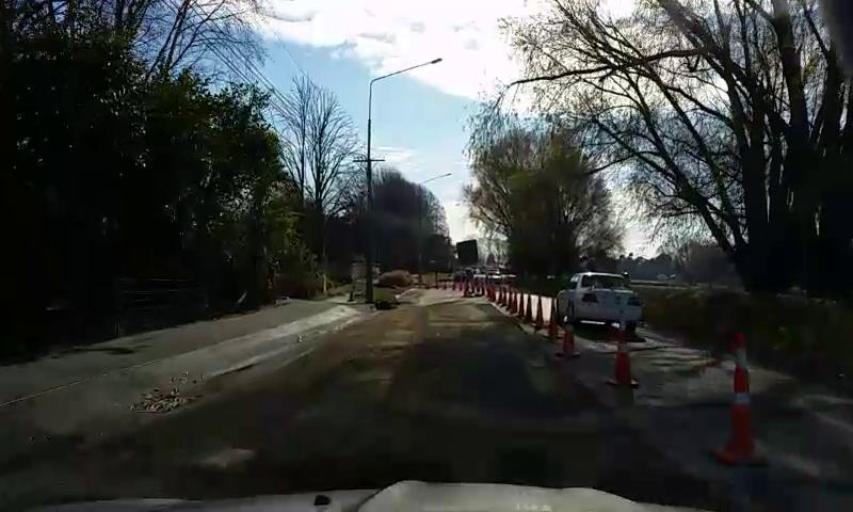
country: NZ
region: Canterbury
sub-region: Christchurch City
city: Christchurch
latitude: -43.5034
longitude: 172.6825
